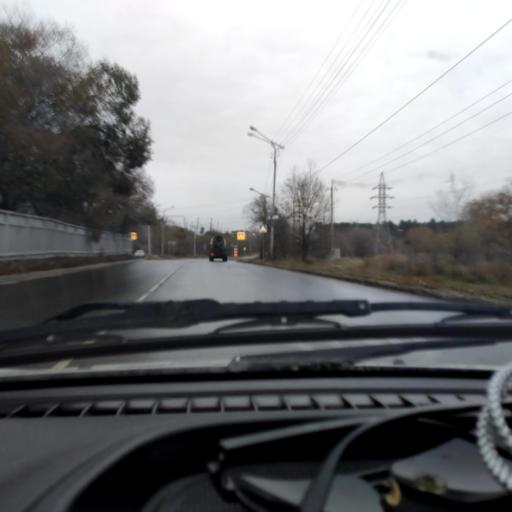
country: RU
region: Samara
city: Zhigulevsk
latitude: 53.4737
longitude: 49.5369
